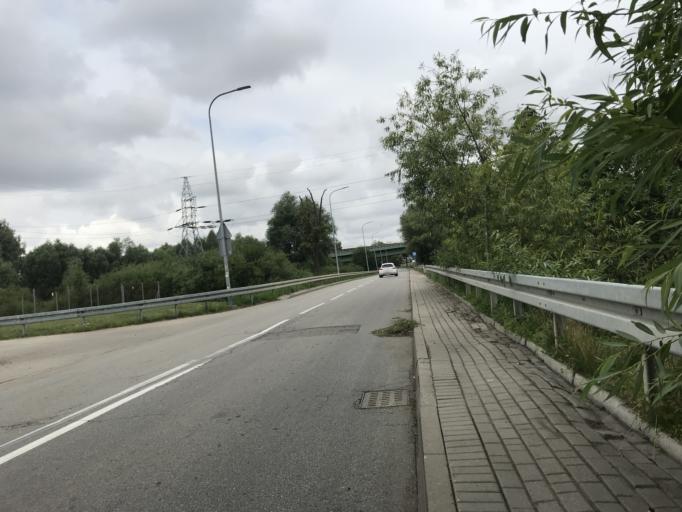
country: PL
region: Warmian-Masurian Voivodeship
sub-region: Powiat elblaski
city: Elblag
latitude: 54.1706
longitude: 19.3873
